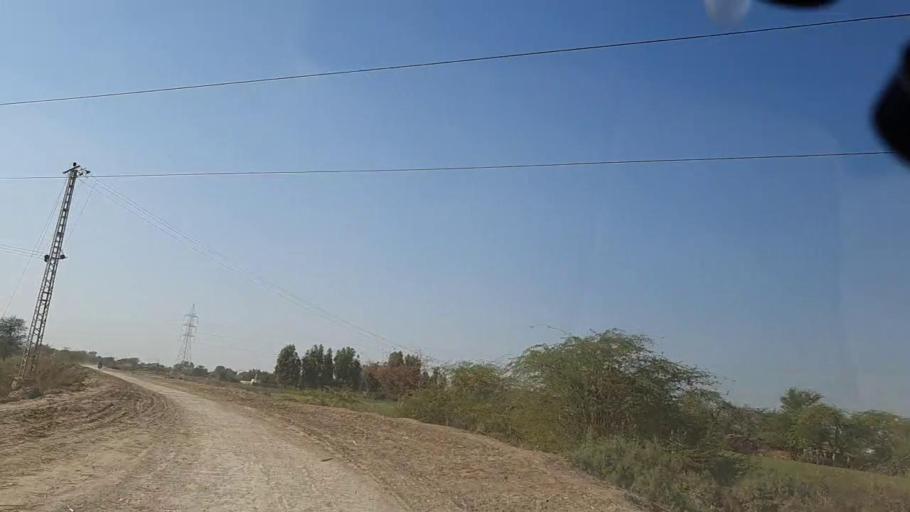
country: PK
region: Sindh
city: Mirpur Khas
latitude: 25.5182
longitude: 68.9308
